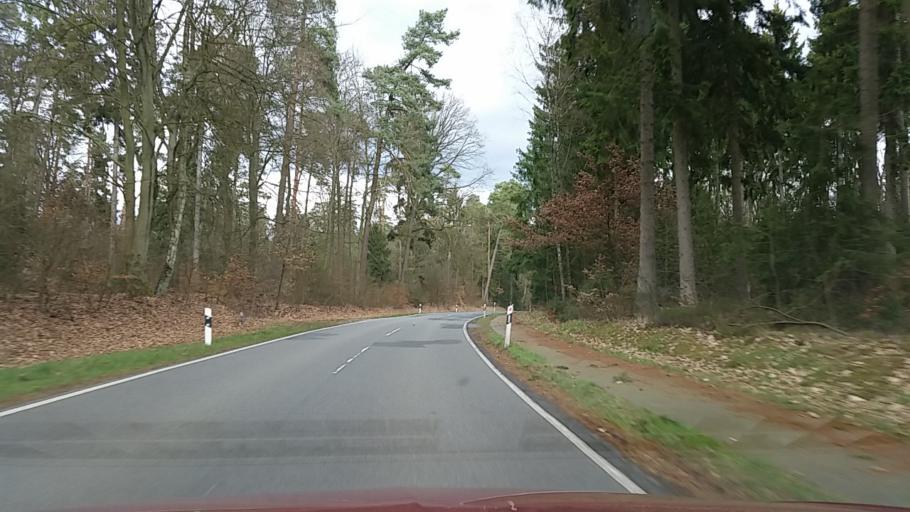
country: DE
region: Lower Saxony
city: Zernien
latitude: 53.0837
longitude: 10.9420
